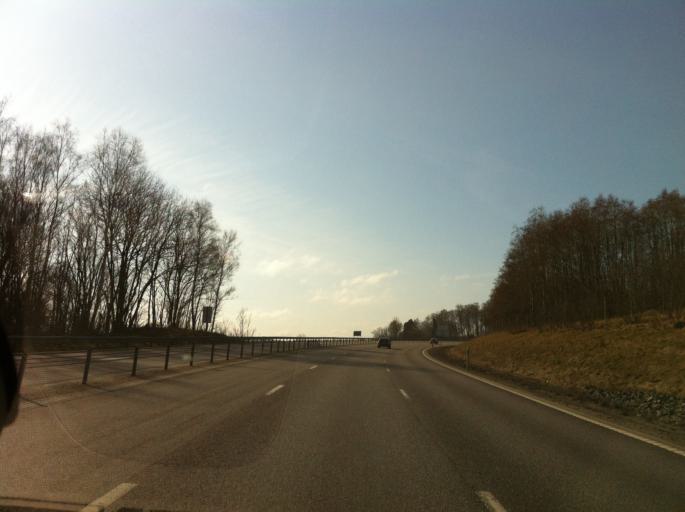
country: SE
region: Joenkoeping
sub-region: Jonkopings Kommun
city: Jonkoping
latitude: 57.7527
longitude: 14.1330
